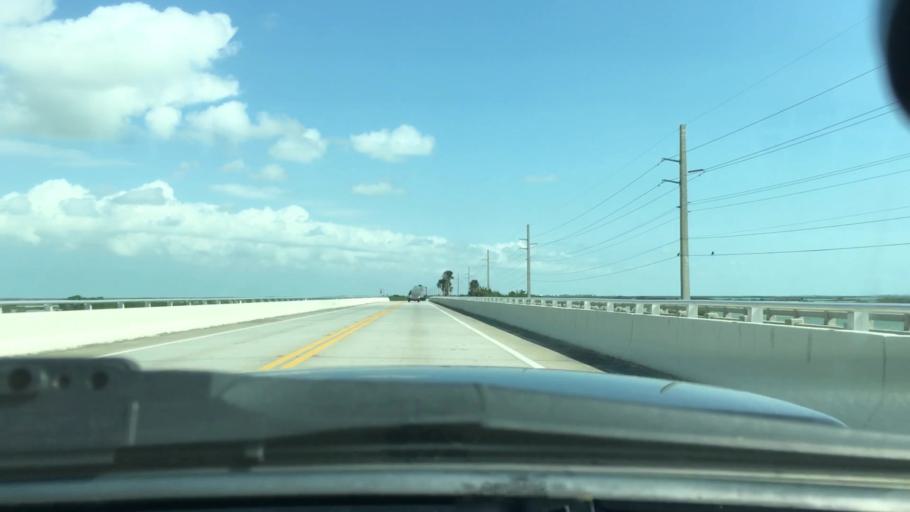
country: US
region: Florida
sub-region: Monroe County
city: Big Coppitt Key
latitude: 24.6052
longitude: -81.6405
